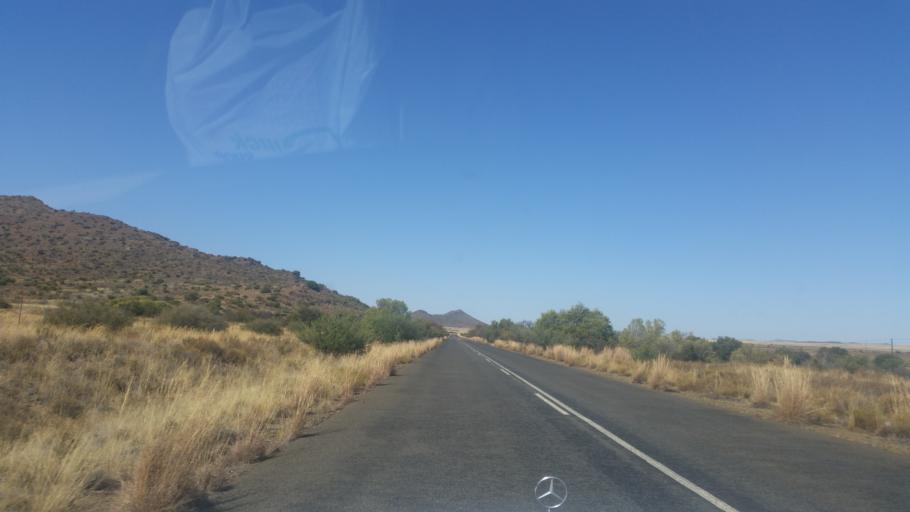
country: ZA
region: Orange Free State
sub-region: Xhariep District Municipality
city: Trompsburg
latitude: -30.5506
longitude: 25.6365
